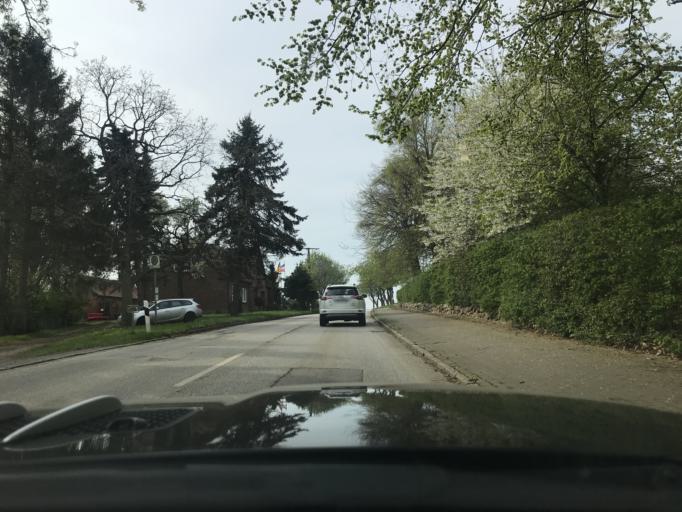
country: DE
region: Schleswig-Holstein
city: Heringsdorf
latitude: 54.2889
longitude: 11.0174
